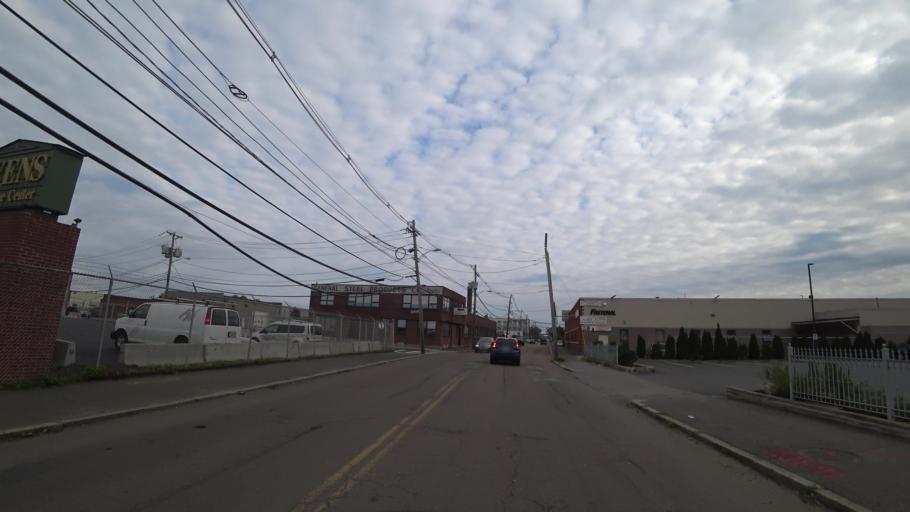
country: US
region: Massachusetts
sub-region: Middlesex County
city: Everett
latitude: 42.4005
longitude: -71.0504
